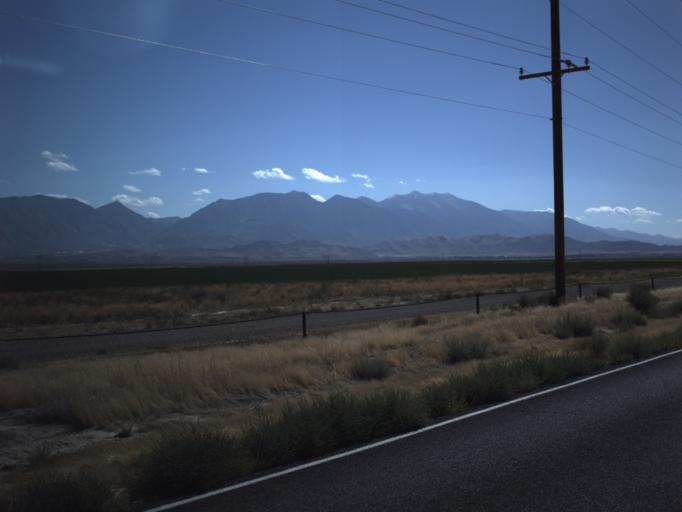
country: US
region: Utah
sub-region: Utah County
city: Genola
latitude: 40.0600
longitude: -111.9584
